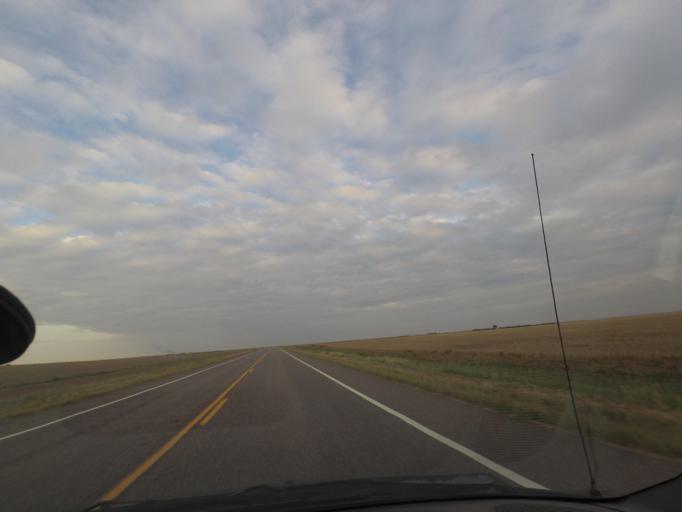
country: US
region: Kansas
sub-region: Cheyenne County
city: Saint Francis
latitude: 39.7470
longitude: -102.0631
